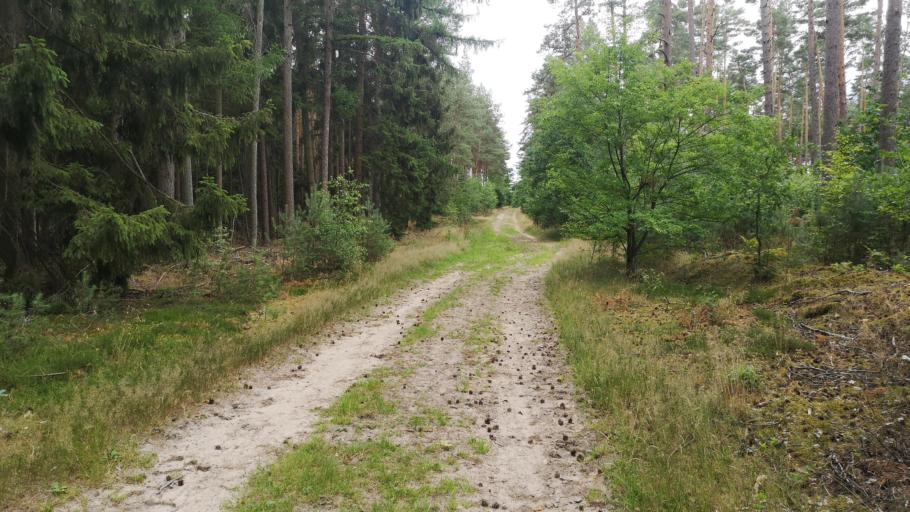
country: DE
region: Lower Saxony
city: Thomasburg
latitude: 53.2341
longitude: 10.6933
